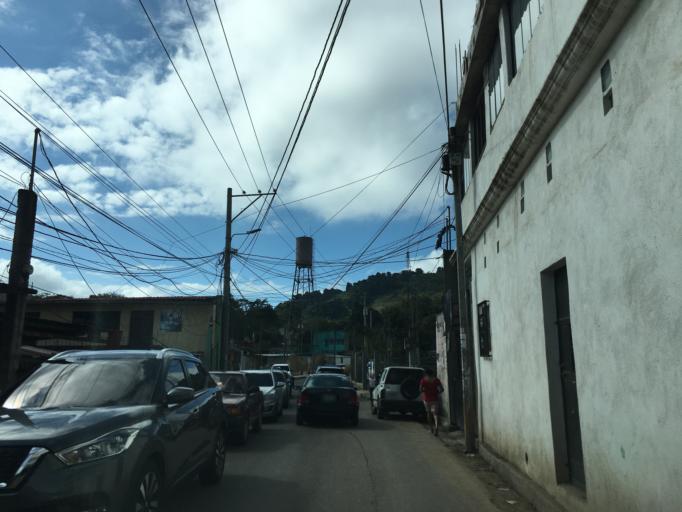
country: GT
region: Guatemala
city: San Jose Pinula
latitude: 14.5592
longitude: -90.4372
